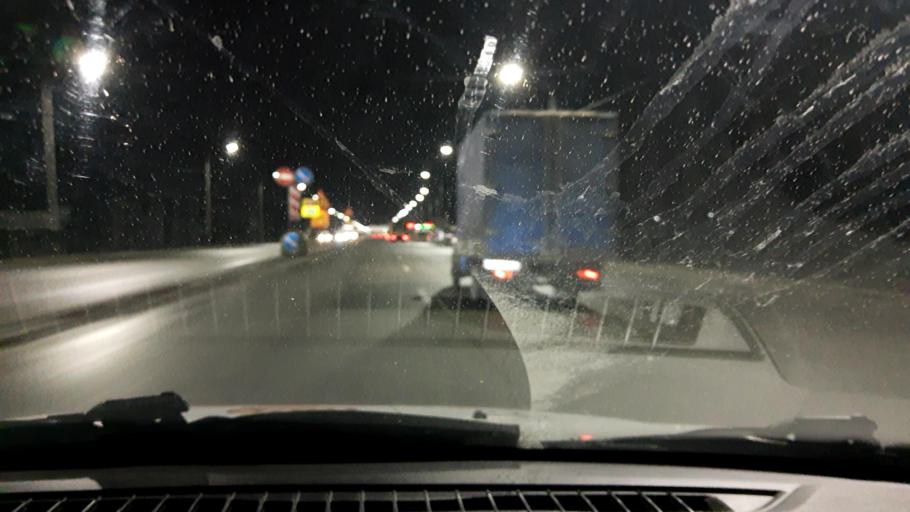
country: RU
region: Nizjnij Novgorod
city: Babino
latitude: 56.3050
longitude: 43.6305
